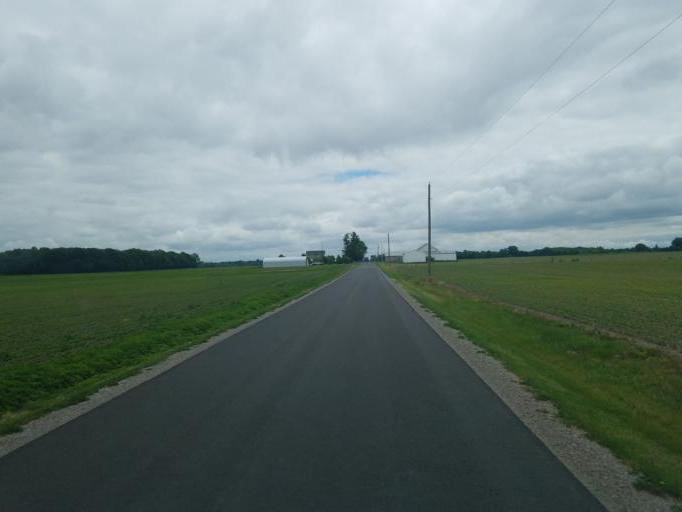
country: US
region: Ohio
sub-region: Wyandot County
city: Upper Sandusky
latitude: 40.7748
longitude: -83.1611
